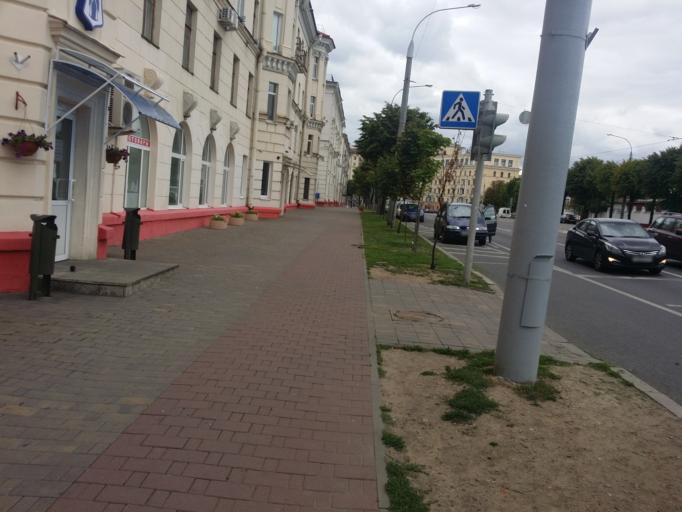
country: BY
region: Minsk
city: Minsk
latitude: 53.9129
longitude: 27.5757
